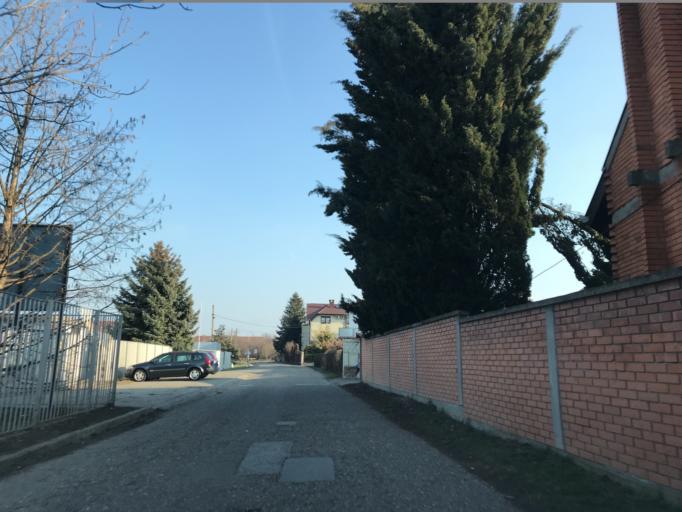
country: RS
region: Autonomna Pokrajina Vojvodina
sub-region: Juznobacki Okrug
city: Novi Sad
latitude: 45.2260
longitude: 19.8547
